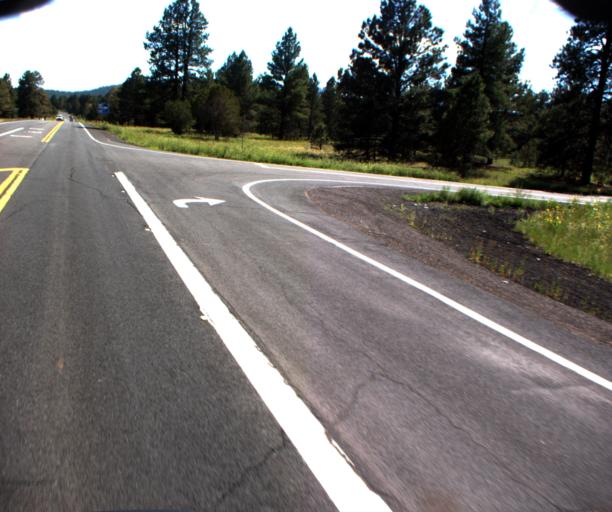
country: US
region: Arizona
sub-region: Coconino County
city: Williams
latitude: 35.2716
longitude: -112.1488
